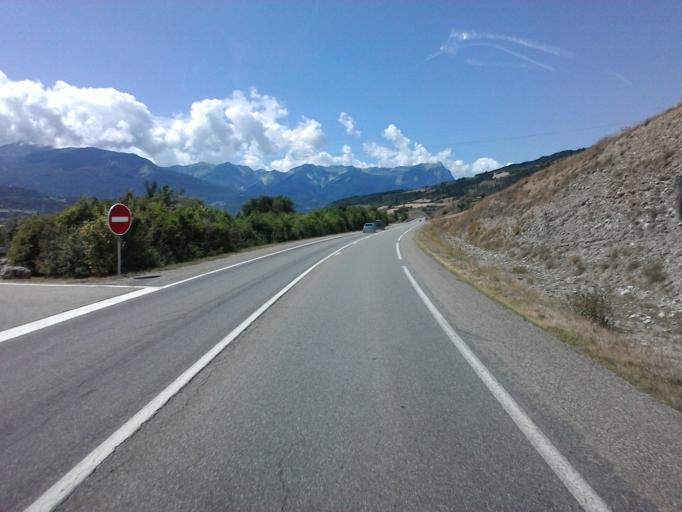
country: FR
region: Provence-Alpes-Cote d'Azur
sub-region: Departement des Hautes-Alpes
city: Embrun
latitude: 44.5979
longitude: 6.5244
